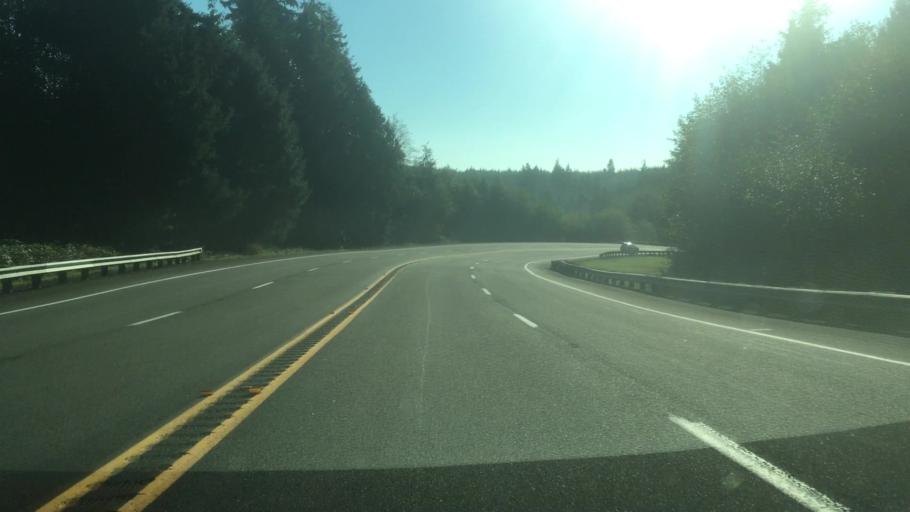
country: US
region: Washington
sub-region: Pacific County
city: South Bend
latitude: 46.6811
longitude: -123.8933
